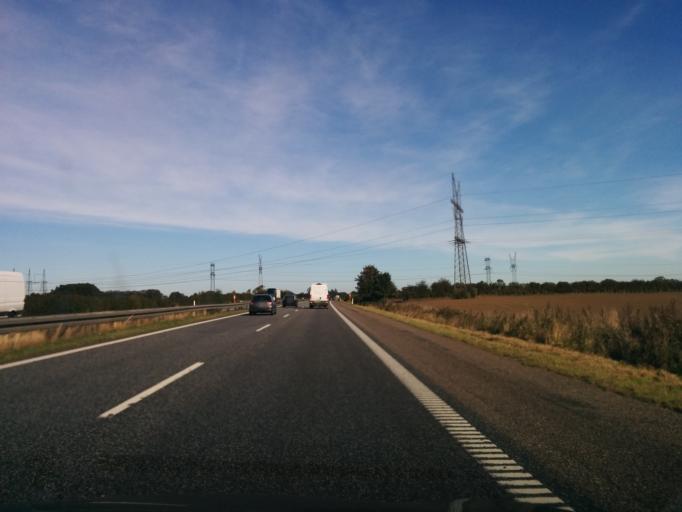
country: DK
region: South Denmark
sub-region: Fredericia Kommune
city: Taulov
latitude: 55.5588
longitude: 9.5488
